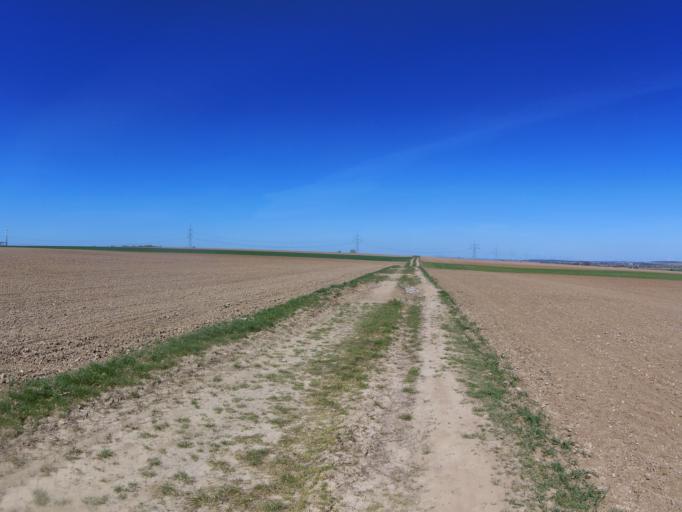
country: DE
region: Bavaria
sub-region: Regierungsbezirk Unterfranken
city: Biebelried
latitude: 49.8014
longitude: 10.0836
